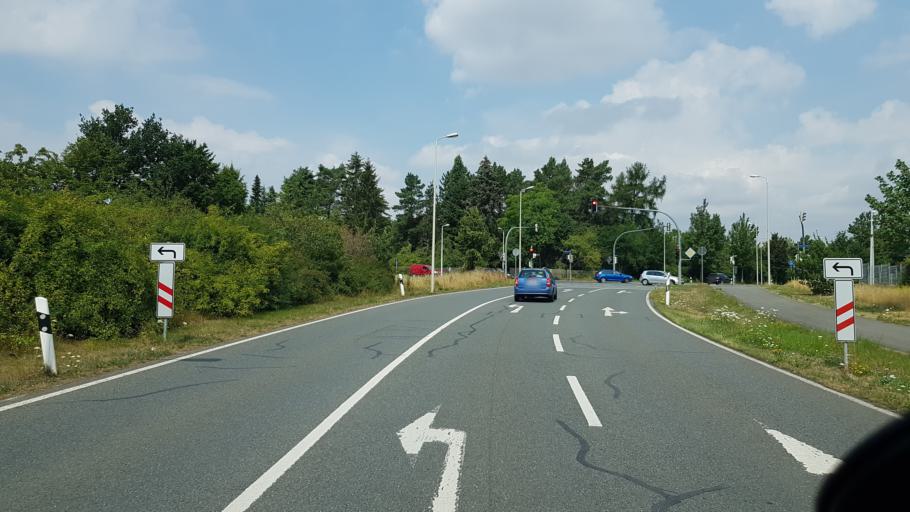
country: DE
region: Saxony
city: Lichtentanne
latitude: 50.6853
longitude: 12.4591
